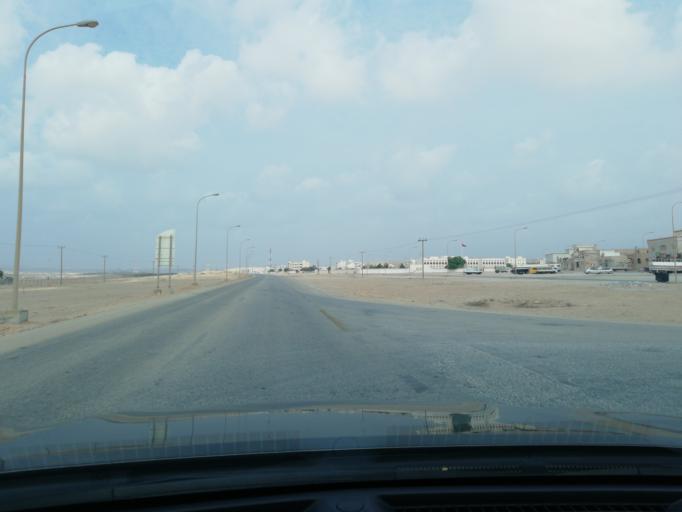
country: OM
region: Zufar
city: Salalah
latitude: 16.9492
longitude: 53.9735
